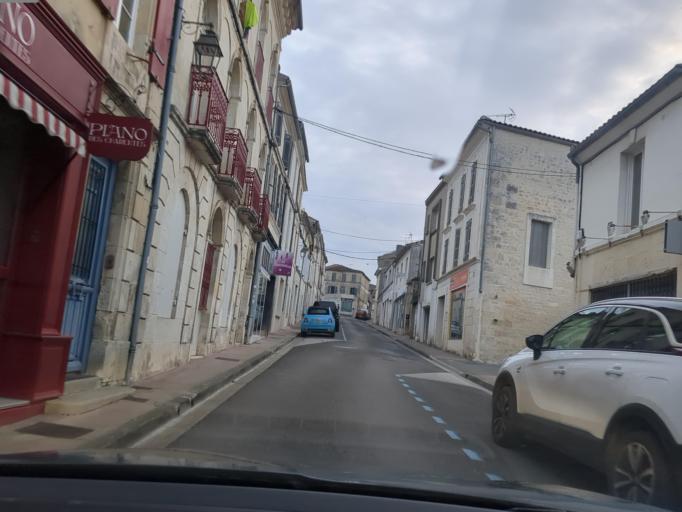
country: FR
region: Poitou-Charentes
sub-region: Departement de la Charente-Maritime
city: Jonzac
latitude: 45.4457
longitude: -0.4340
